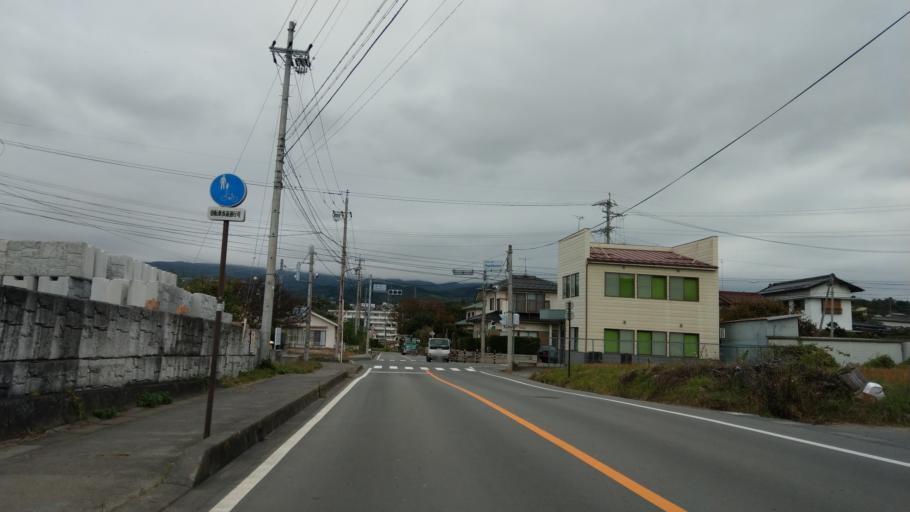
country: JP
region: Nagano
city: Komoro
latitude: 36.3155
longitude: 138.4285
